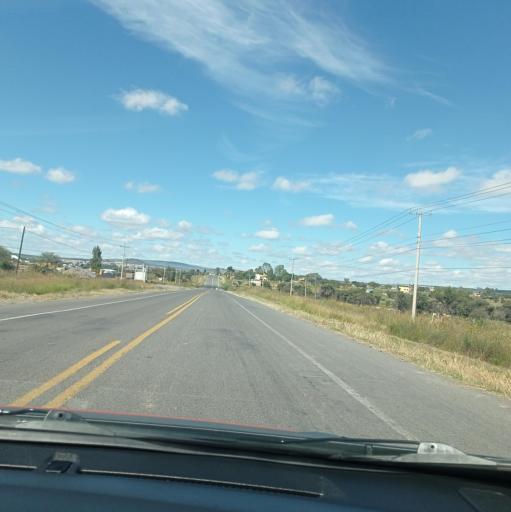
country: MX
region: Jalisco
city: San Miguel el Alto
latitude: 21.0230
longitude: -102.3605
